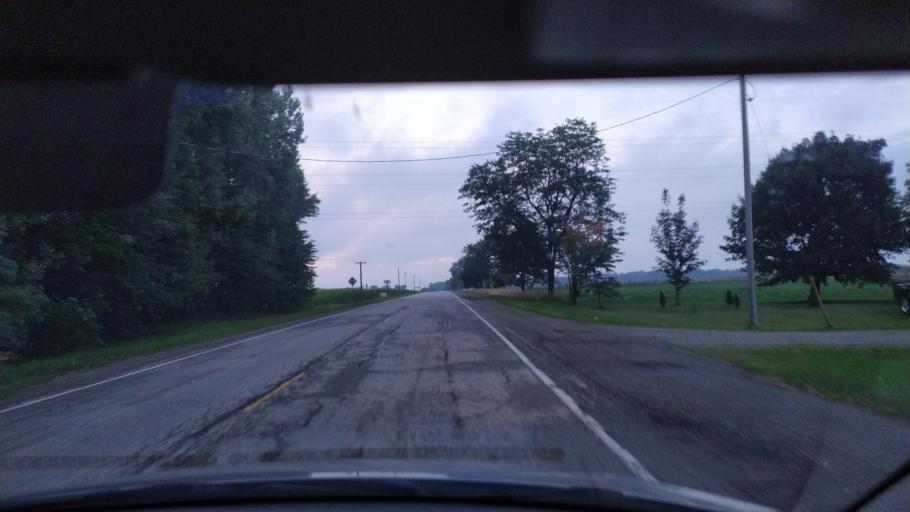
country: CA
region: Ontario
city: Kitchener
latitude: 43.3511
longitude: -80.6961
